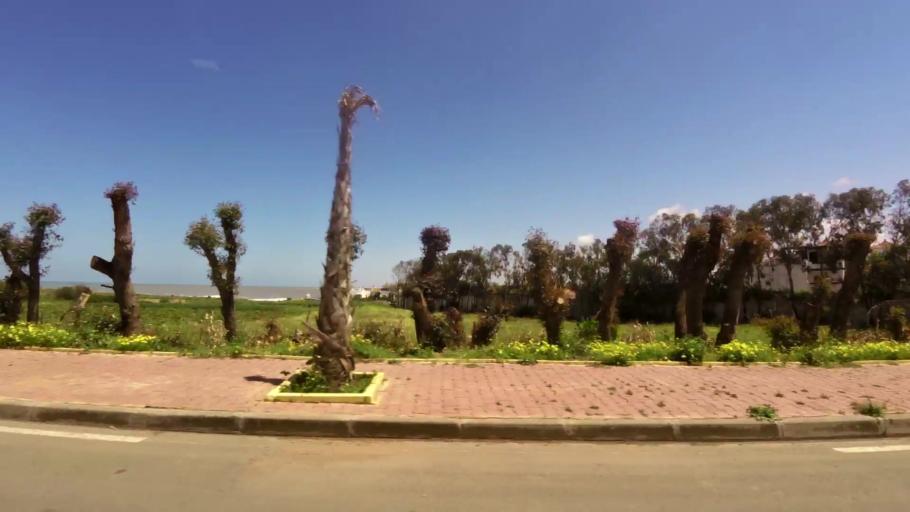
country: MA
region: Grand Casablanca
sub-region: Nouaceur
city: Dar Bouazza
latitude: 33.5300
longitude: -7.8208
